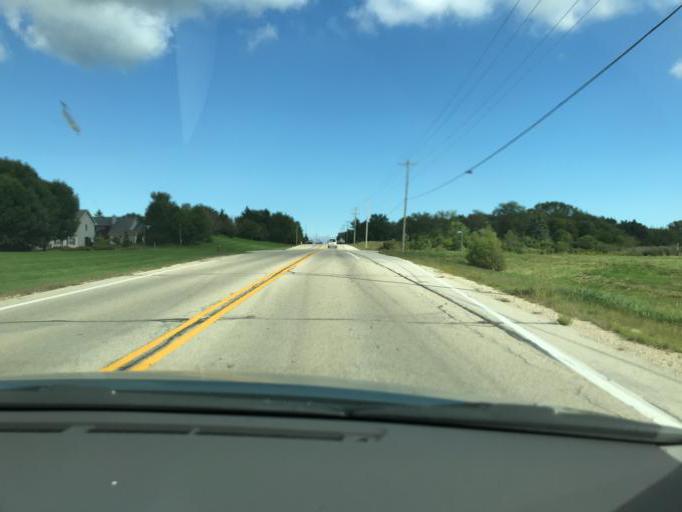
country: US
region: Wisconsin
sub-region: Kenosha County
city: Pleasant Prairie
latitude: 42.5229
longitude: -87.8866
